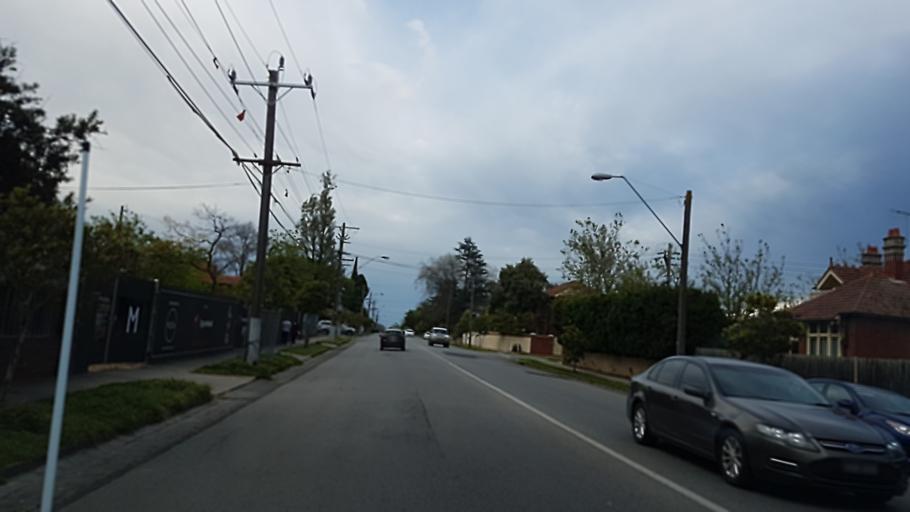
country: AU
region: Victoria
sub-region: Stonnington
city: Malvern East
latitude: -37.8693
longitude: 145.0495
